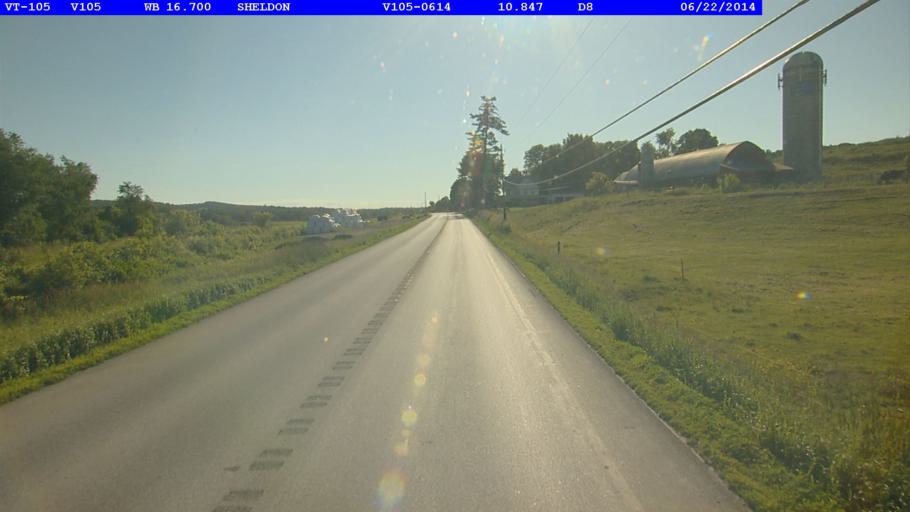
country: US
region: Vermont
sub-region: Franklin County
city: Enosburg Falls
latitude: 44.9076
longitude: -72.8229
